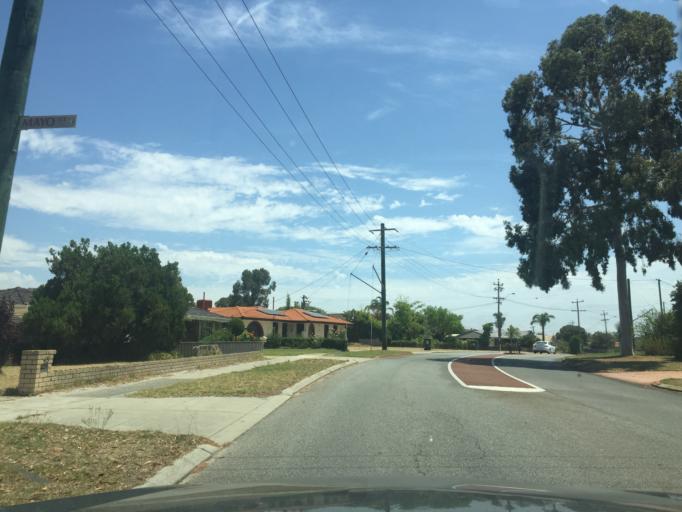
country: AU
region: Western Australia
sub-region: Canning
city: Ferndale
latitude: -32.0426
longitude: 115.9121
